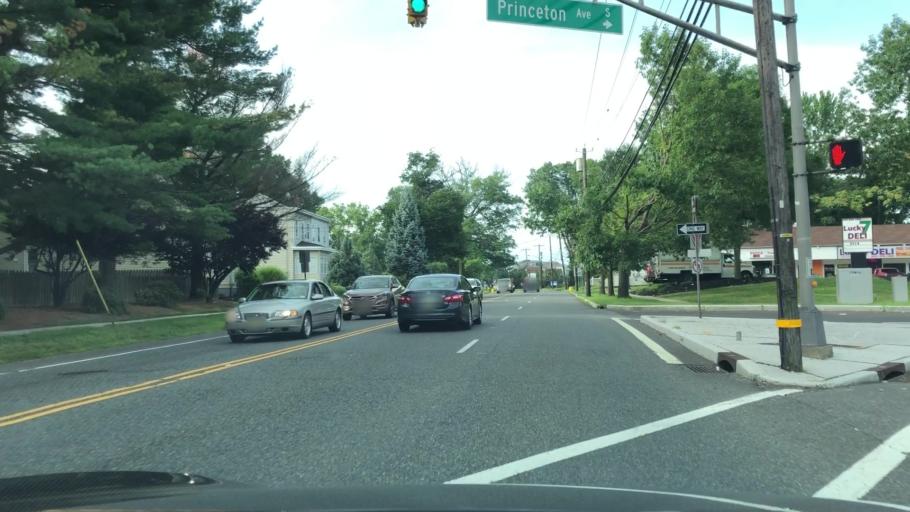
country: US
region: New Jersey
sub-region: Mercer County
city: Prospect Park
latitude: 40.2497
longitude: -74.7426
